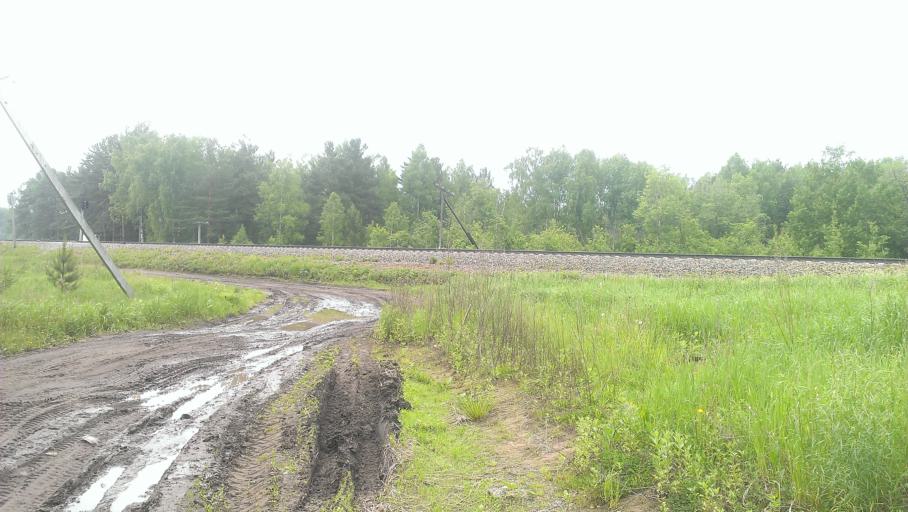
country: RU
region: Altai Krai
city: Bayunovskiye Klyuchi
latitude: 53.3386
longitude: 84.1004
